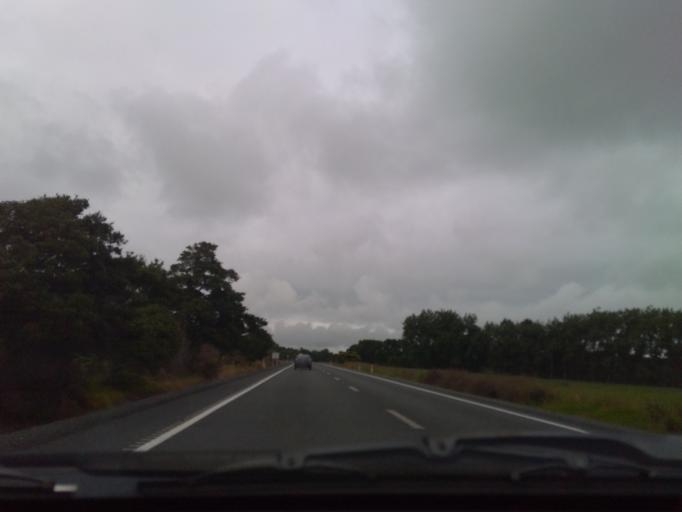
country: NZ
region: Northland
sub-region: Whangarei
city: Ruakaka
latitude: -35.8626
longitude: 174.3933
